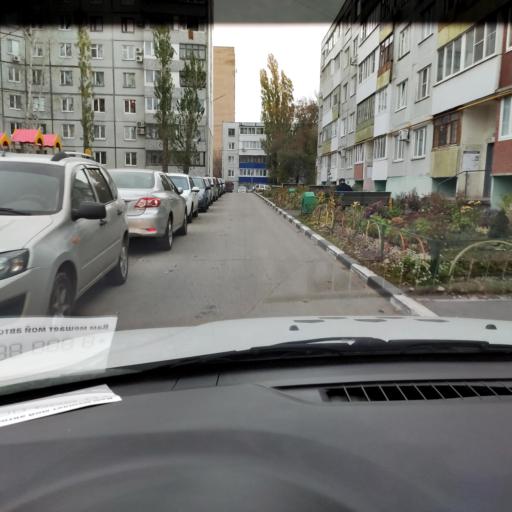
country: RU
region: Samara
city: Zhigulevsk
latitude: 53.4851
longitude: 49.4684
